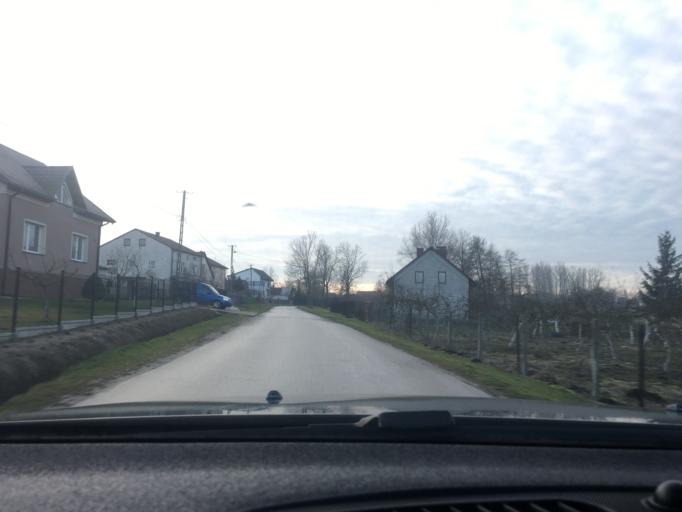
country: PL
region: Swietokrzyskie
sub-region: Powiat jedrzejowski
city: Imielno
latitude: 50.6275
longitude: 20.4040
